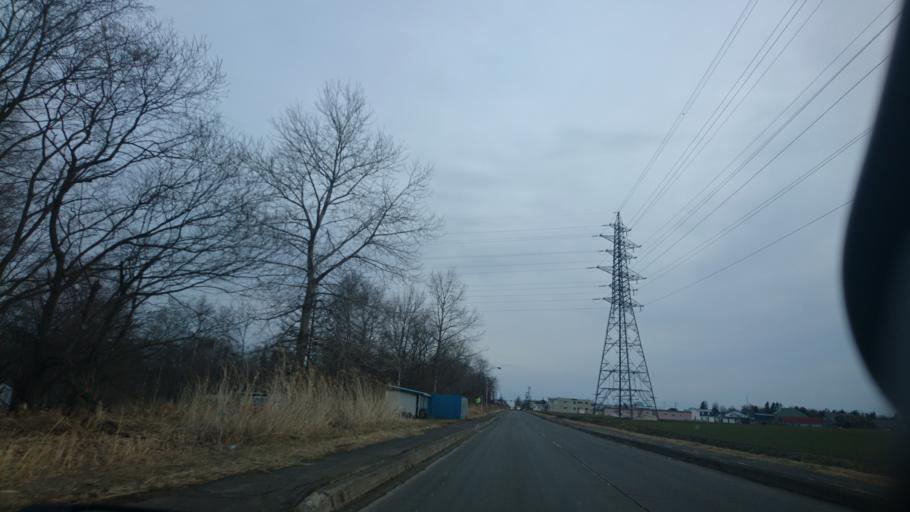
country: JP
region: Hokkaido
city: Otofuke
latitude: 42.9753
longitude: 143.1983
